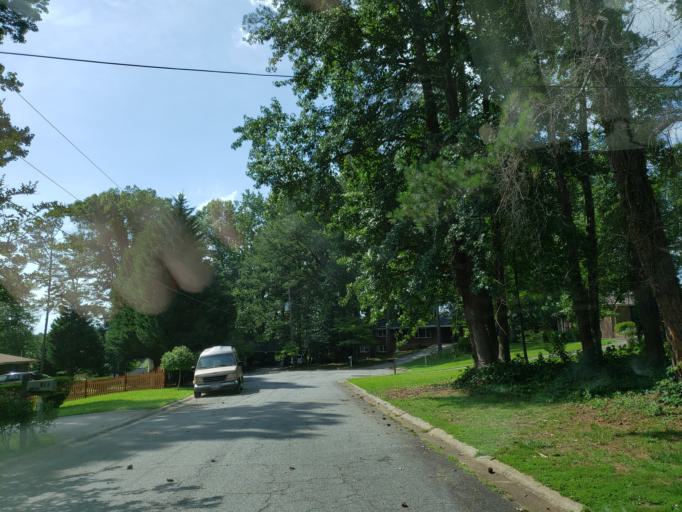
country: US
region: Georgia
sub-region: Cobb County
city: Smyrna
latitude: 33.8741
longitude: -84.5394
